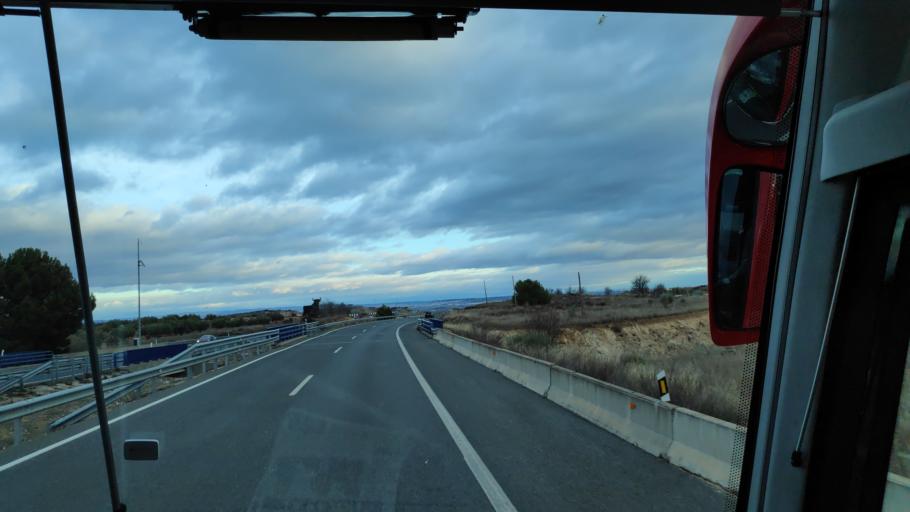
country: ES
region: Madrid
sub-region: Provincia de Madrid
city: Villarejo de Salvanes
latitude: 40.1510
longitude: -3.2366
